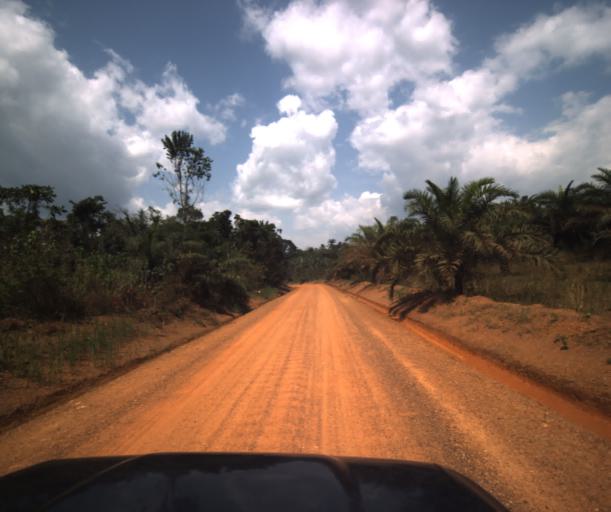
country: CM
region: Centre
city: Akono
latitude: 3.5501
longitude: 11.0565
